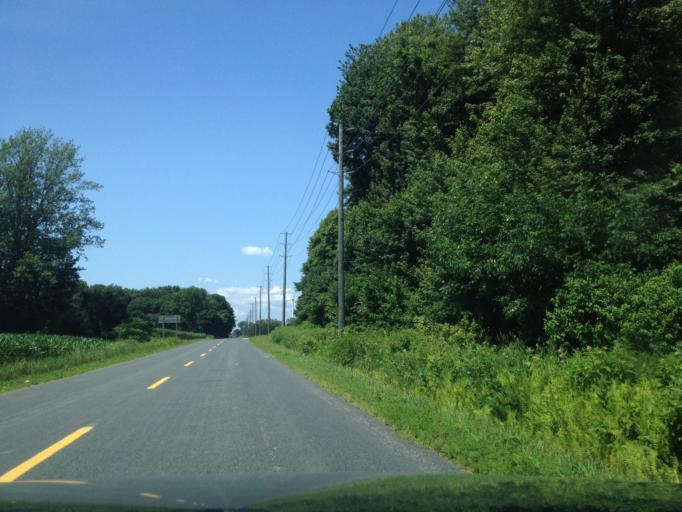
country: CA
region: Ontario
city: Aylmer
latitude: 42.6391
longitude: -80.7243
